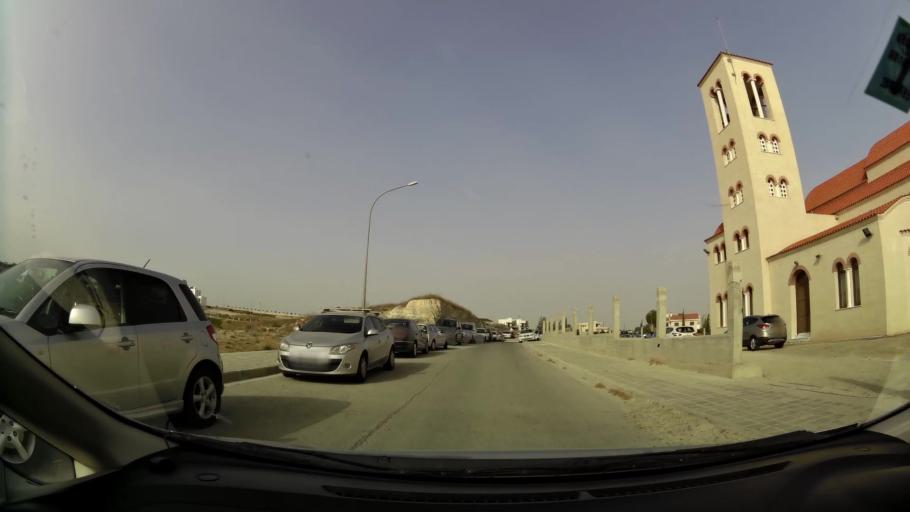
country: CY
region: Lefkosia
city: Geri
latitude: 35.0712
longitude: 33.3850
